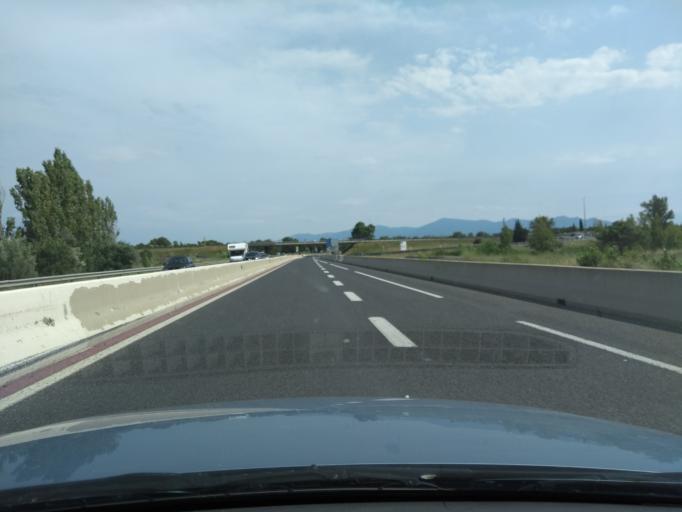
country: FR
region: Languedoc-Roussillon
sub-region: Departement des Pyrenees-Orientales
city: Toulouges
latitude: 42.6730
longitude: 2.8561
